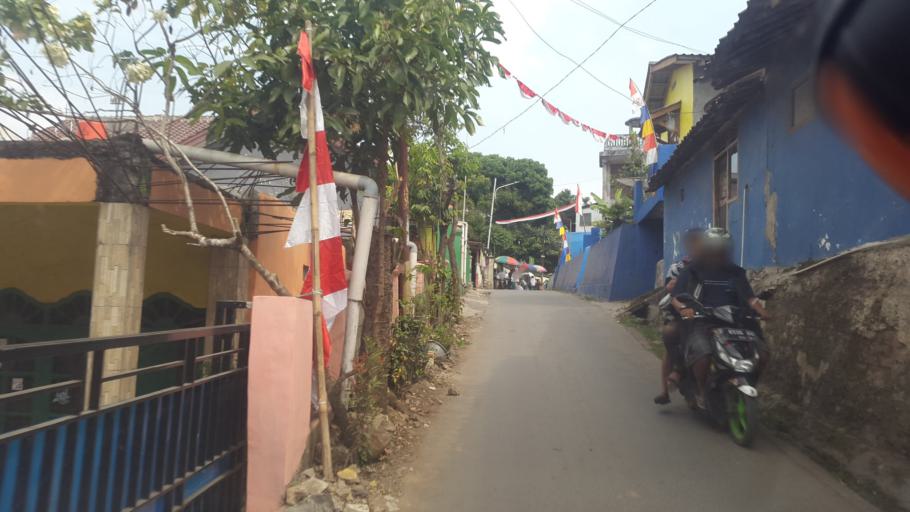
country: ID
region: West Java
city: Cicurug
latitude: -6.7798
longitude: 106.7855
